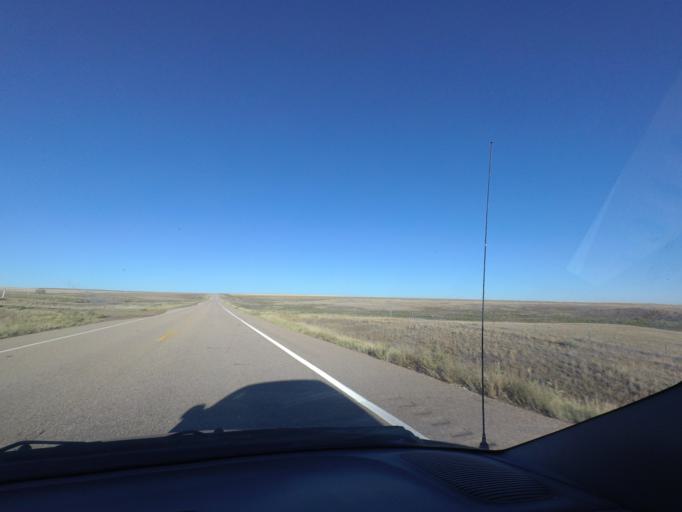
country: US
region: Colorado
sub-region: Arapahoe County
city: Byers
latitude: 39.7400
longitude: -103.7565
